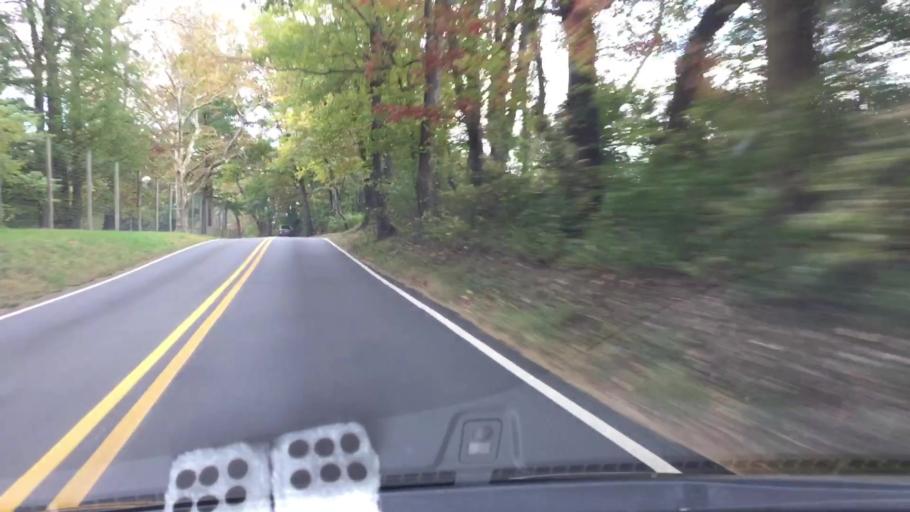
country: US
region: Pennsylvania
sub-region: Delaware County
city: Lima
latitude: 39.9323
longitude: -75.4383
